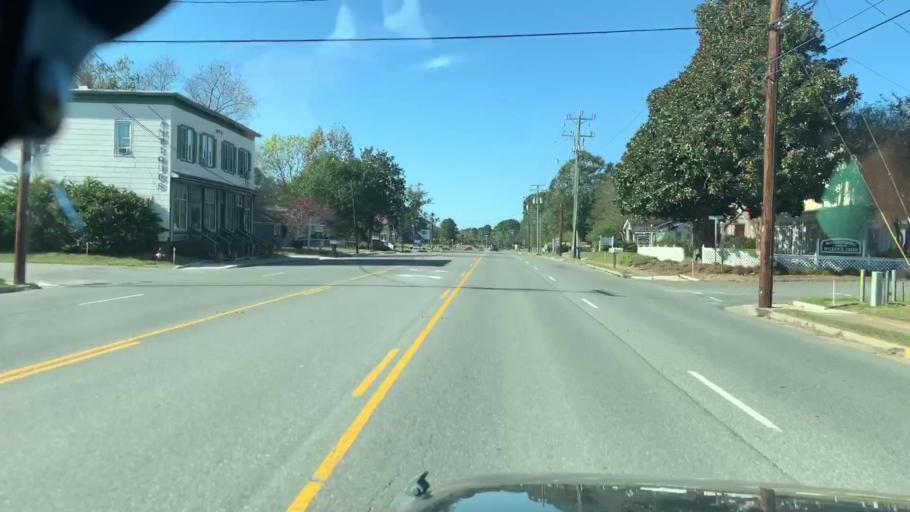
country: US
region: Virginia
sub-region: James City County
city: Williamsburg
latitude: 37.3680
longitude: -76.7705
